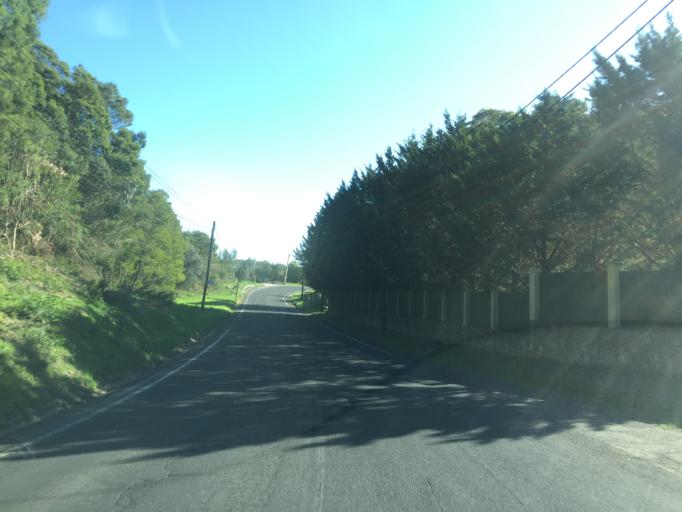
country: PT
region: Lisbon
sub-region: Sintra
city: Belas
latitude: 38.7986
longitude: -9.2716
